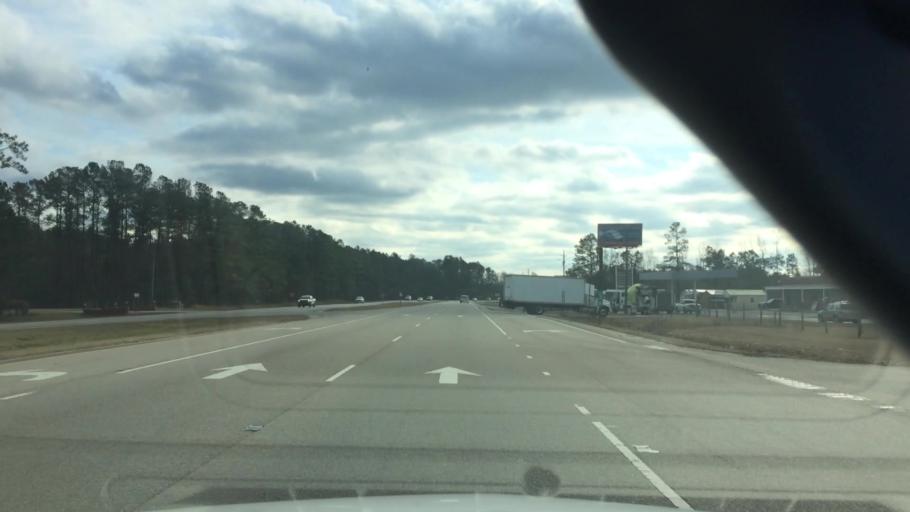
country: US
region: North Carolina
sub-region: Brunswick County
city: Bolivia
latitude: 34.1422
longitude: -78.0939
